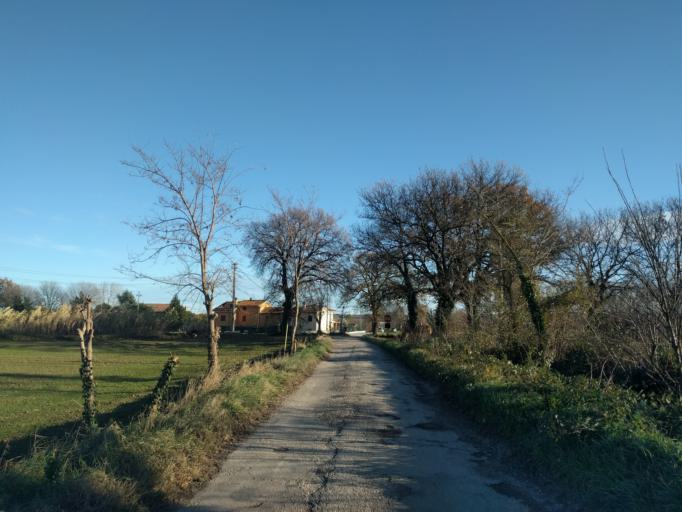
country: IT
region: The Marches
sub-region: Provincia di Pesaro e Urbino
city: Bellocchi
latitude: 43.7965
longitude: 12.9833
